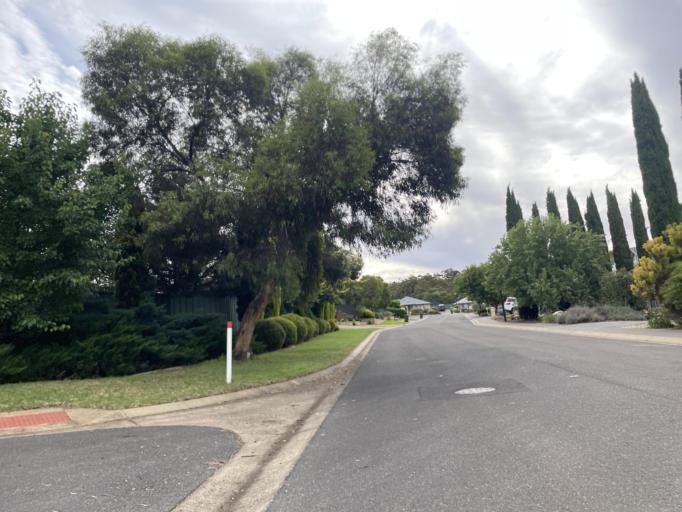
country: AU
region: South Australia
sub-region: Clare and Gilbert Valleys
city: Clare
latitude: -33.8449
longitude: 138.6116
